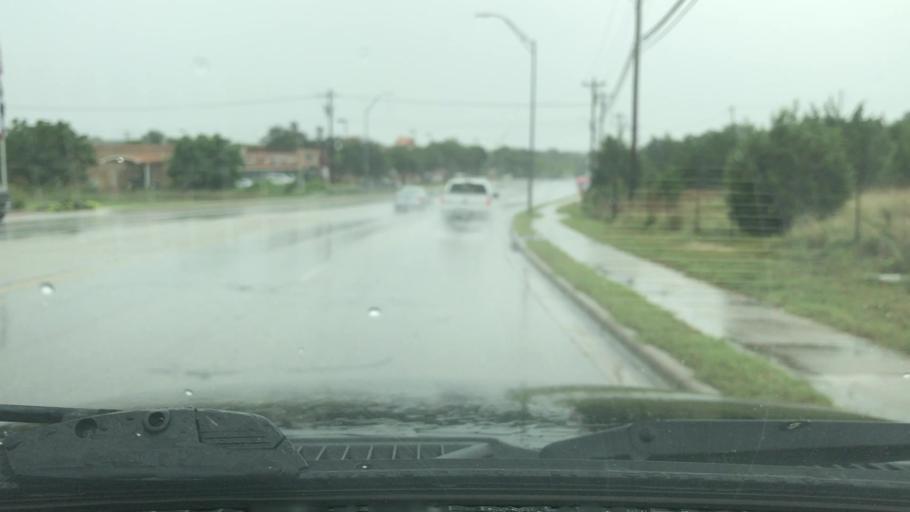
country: US
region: Texas
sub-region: Williamson County
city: Cedar Park
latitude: 30.4993
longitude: -97.8190
